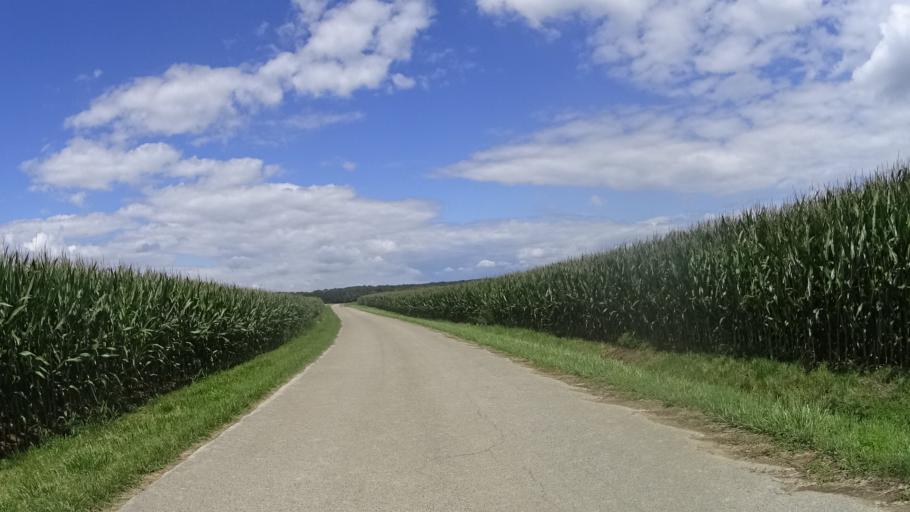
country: FR
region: Champagne-Ardenne
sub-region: Departement de la Haute-Marne
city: Montier-en-Der
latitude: 48.5130
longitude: 4.7747
